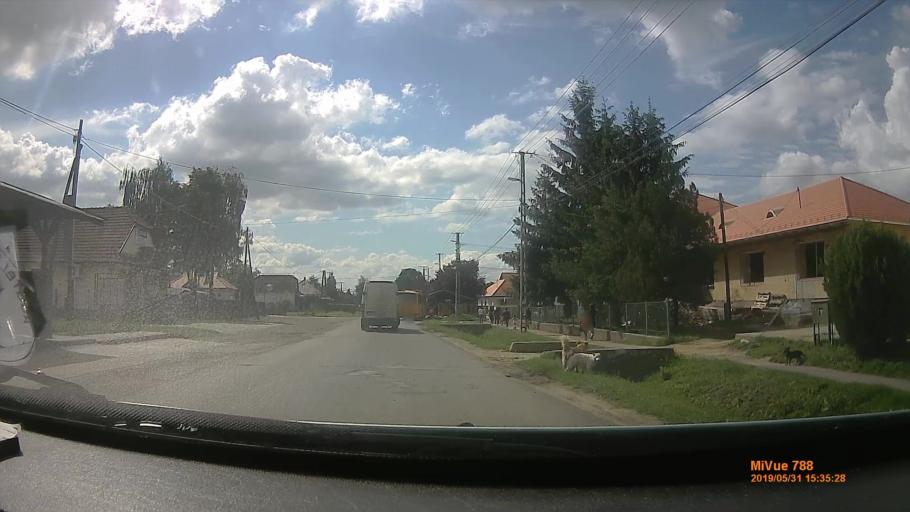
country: HU
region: Borsod-Abauj-Zemplen
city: Prugy
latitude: 48.0805
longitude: 21.2460
